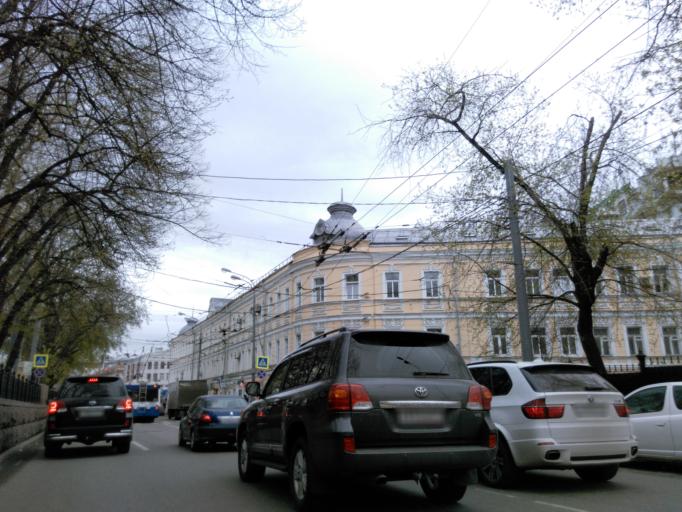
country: RU
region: Moscow
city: Moscow
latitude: 55.7454
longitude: 37.6002
